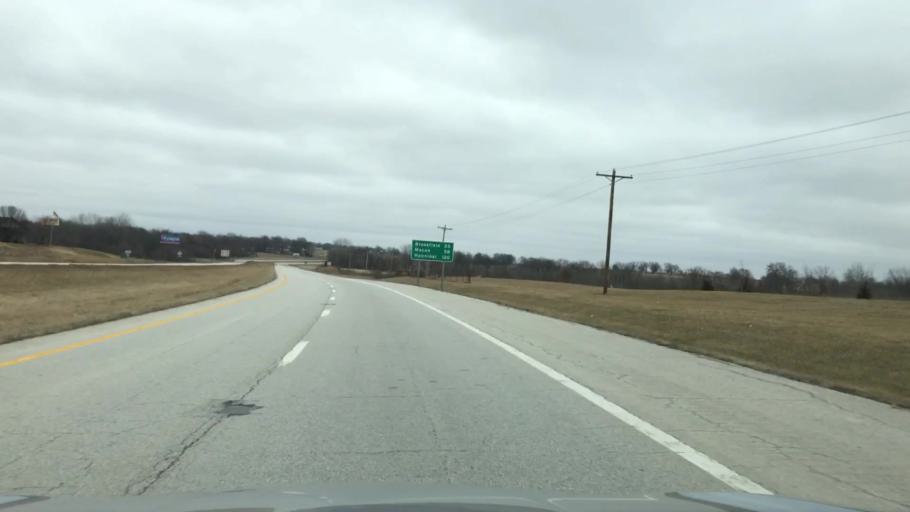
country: US
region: Missouri
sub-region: Livingston County
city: Chillicothe
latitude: 39.7784
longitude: -93.5412
